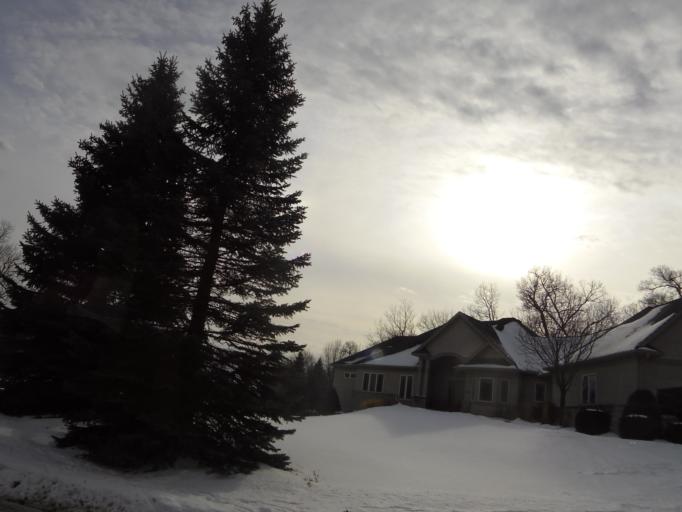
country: US
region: Minnesota
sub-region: Dakota County
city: Lakeville
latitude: 44.6844
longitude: -93.2700
